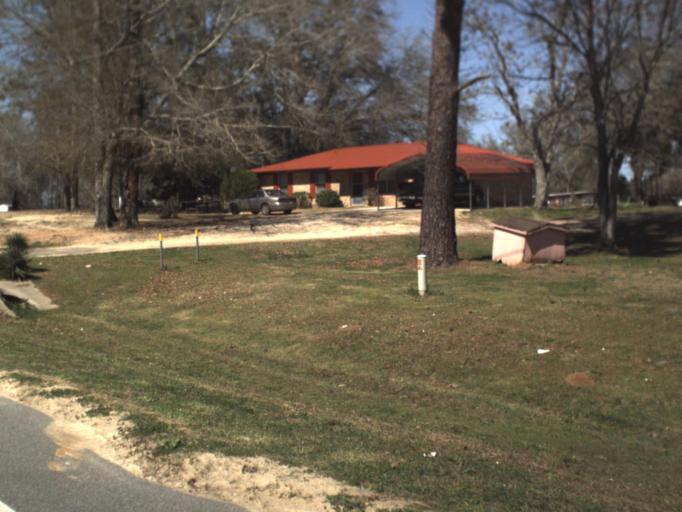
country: US
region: Florida
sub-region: Jackson County
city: Marianna
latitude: 30.8085
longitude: -85.2922
